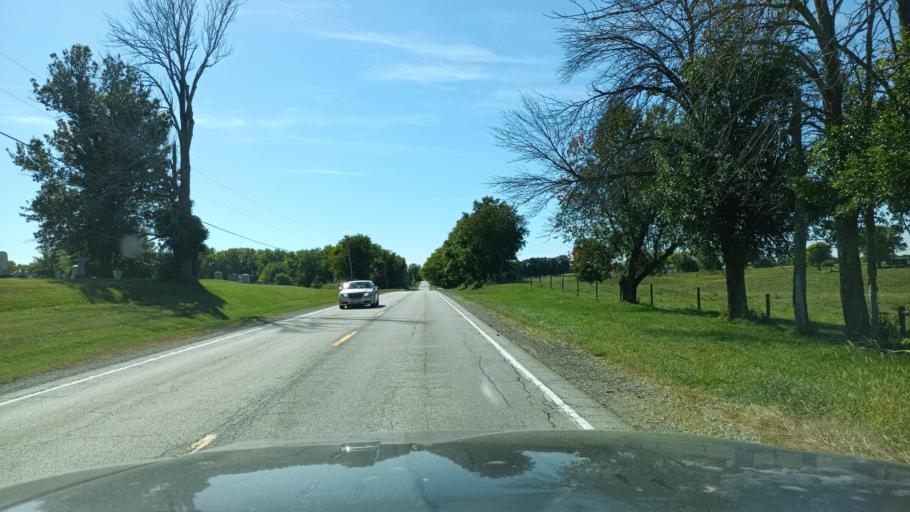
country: US
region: Illinois
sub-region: De Witt County
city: Farmer City
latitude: 40.2308
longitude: -88.6783
